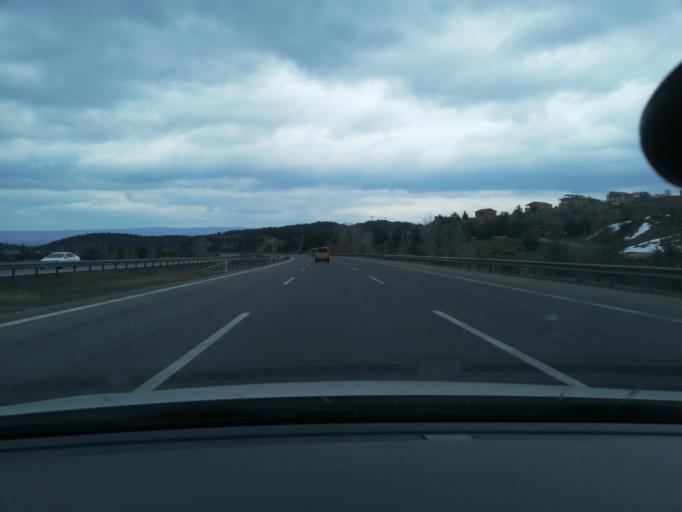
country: TR
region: Bolu
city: Gerede
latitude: 40.6278
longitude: 32.2383
